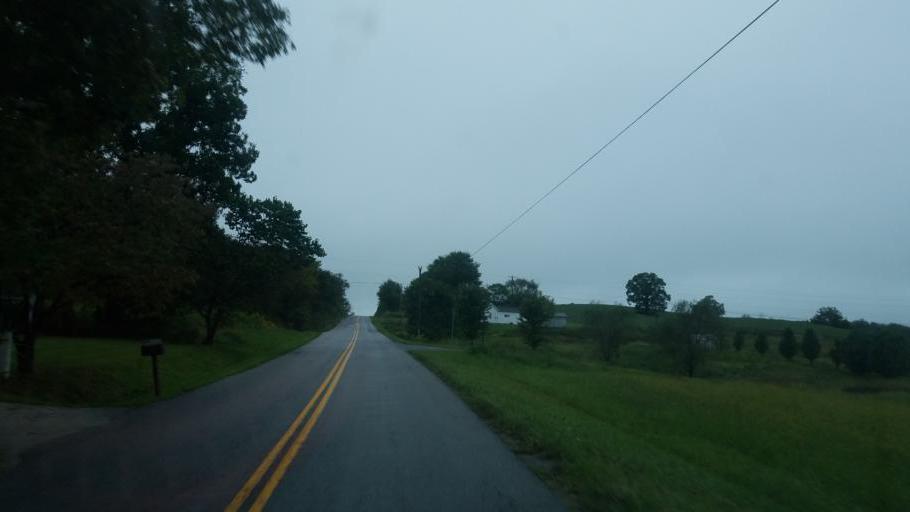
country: US
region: Kentucky
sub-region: Fleming County
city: Flemingsburg
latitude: 38.4081
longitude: -83.6453
